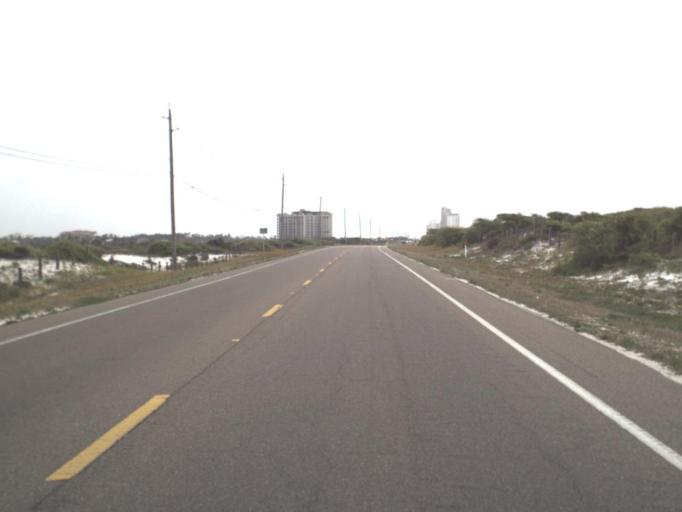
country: US
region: Alabama
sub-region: Baldwin County
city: Orange Beach
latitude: 30.2924
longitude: -87.4634
